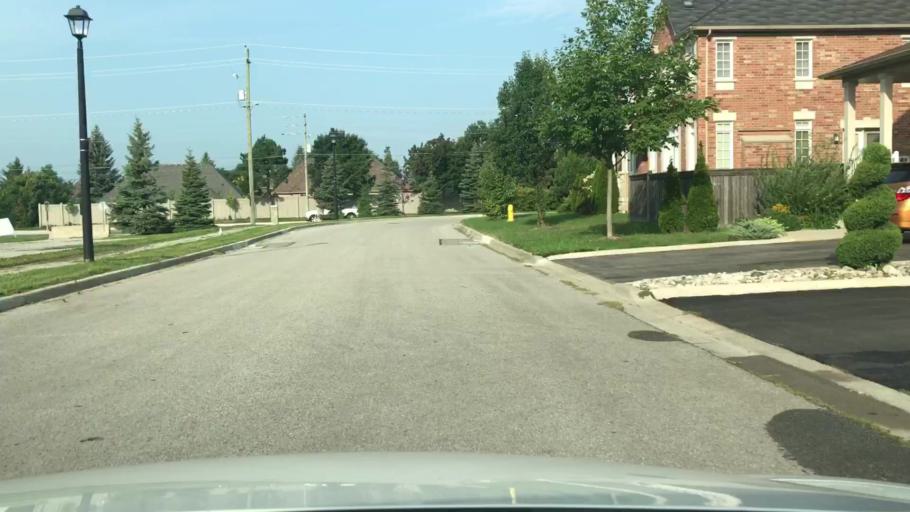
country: CA
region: Ontario
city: Newmarket
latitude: 44.0381
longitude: -79.4243
